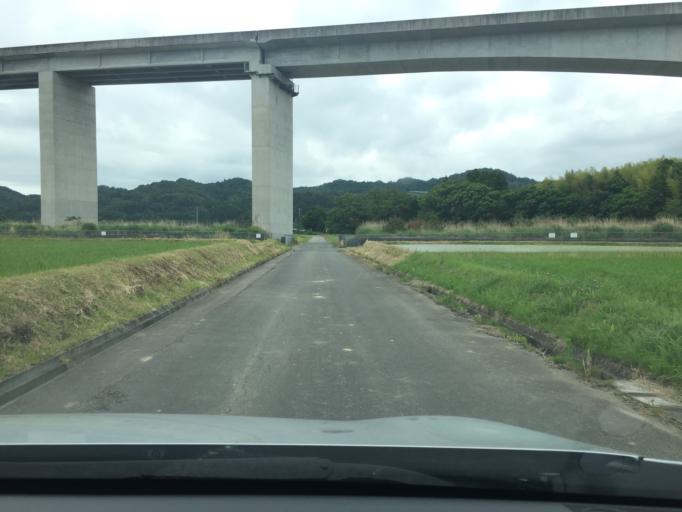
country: JP
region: Fukushima
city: Iwaki
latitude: 37.1180
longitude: 140.9048
